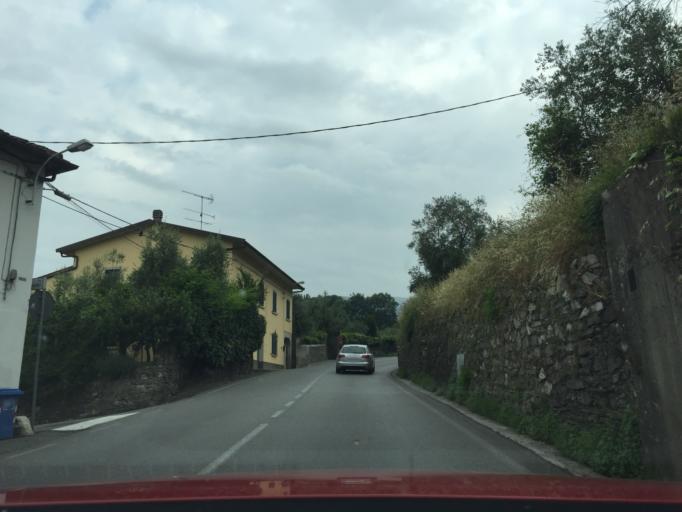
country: IT
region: Tuscany
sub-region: Provincia di Pistoia
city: Serravalle Pistoiese
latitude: 43.9012
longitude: 10.8256
